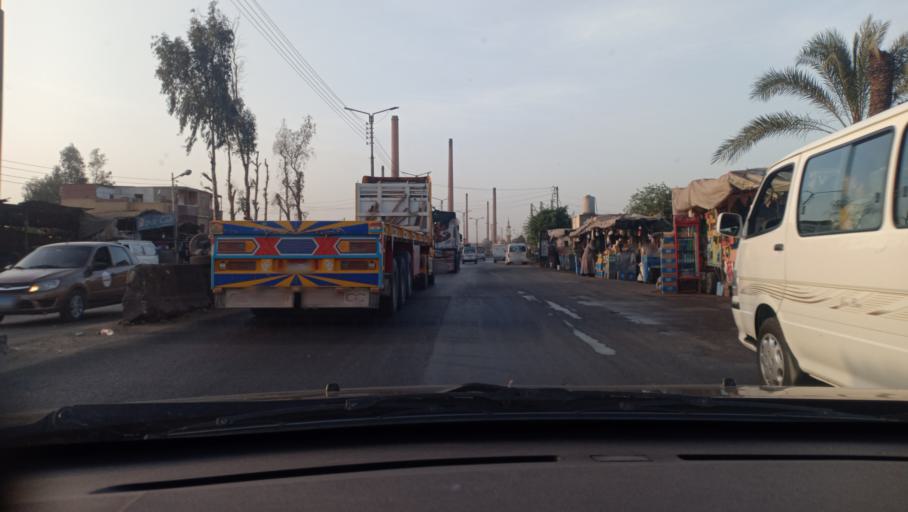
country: EG
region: Muhafazat al Gharbiyah
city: Zifta
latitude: 30.6075
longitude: 31.2753
